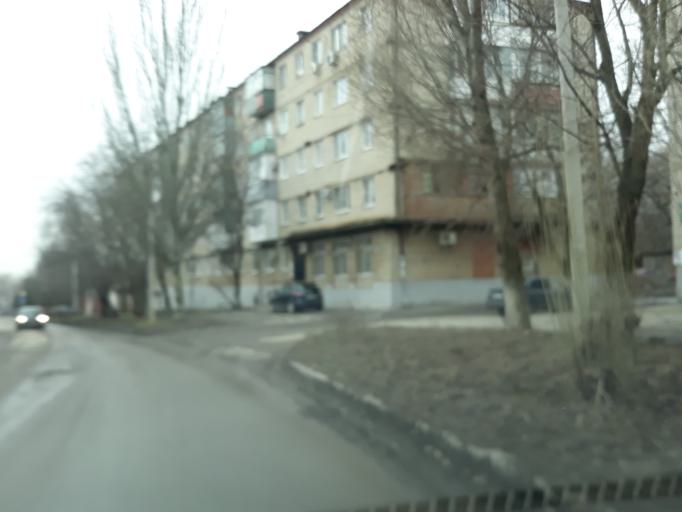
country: RU
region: Rostov
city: Taganrog
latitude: 47.2073
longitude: 38.8982
